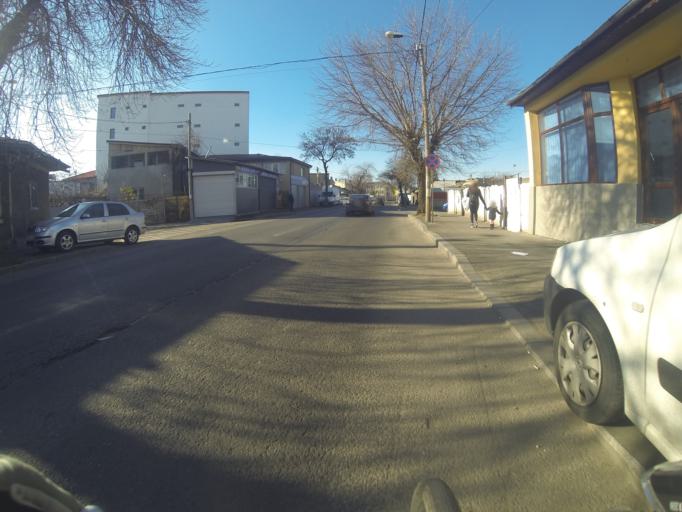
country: RO
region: Bucuresti
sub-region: Municipiul Bucuresti
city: Bucuresti
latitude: 44.3991
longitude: 26.0812
